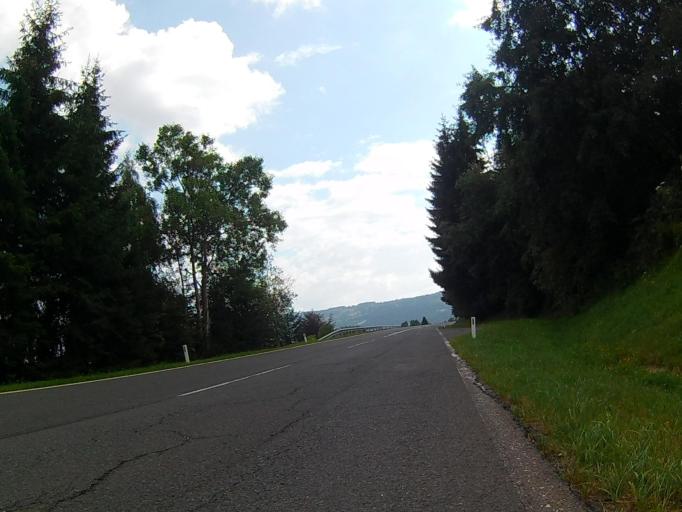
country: AT
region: Styria
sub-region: Politischer Bezirk Deutschlandsberg
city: Soboth
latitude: 46.6825
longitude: 15.0527
